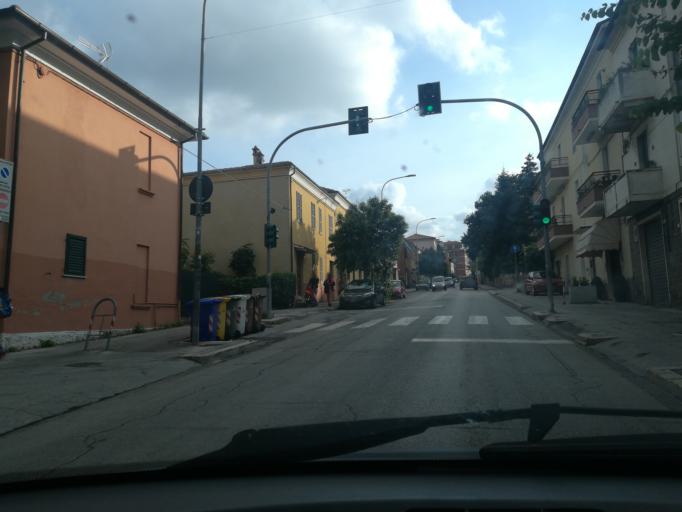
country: IT
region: The Marches
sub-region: Provincia di Macerata
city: Macerata
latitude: 43.3045
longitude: 13.4613
